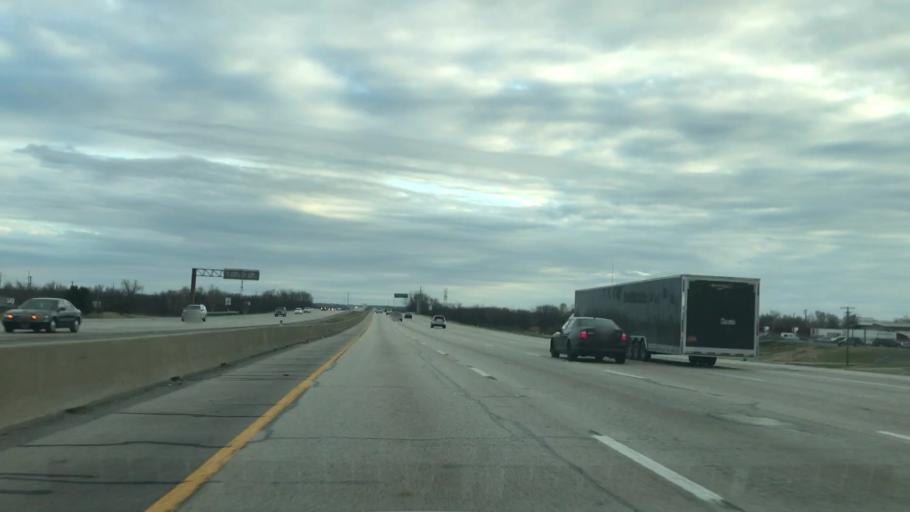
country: US
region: Texas
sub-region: Dallas County
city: Irving
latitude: 32.7977
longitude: -96.9215
